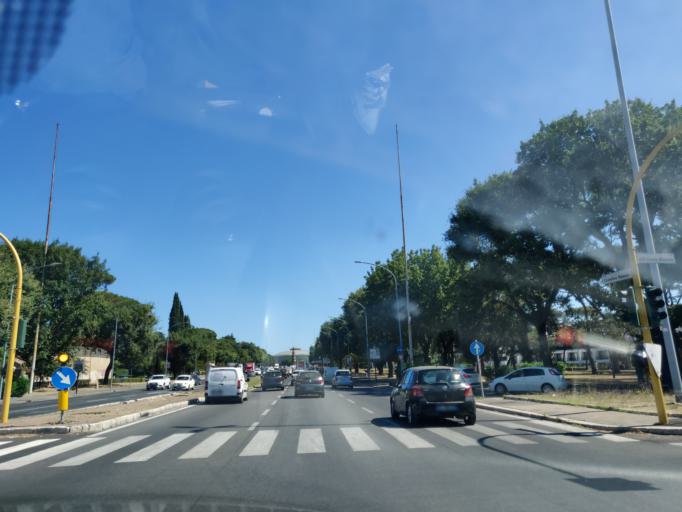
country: IT
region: Latium
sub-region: Citta metropolitana di Roma Capitale
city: Selcetta
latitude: 41.8185
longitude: 12.4631
